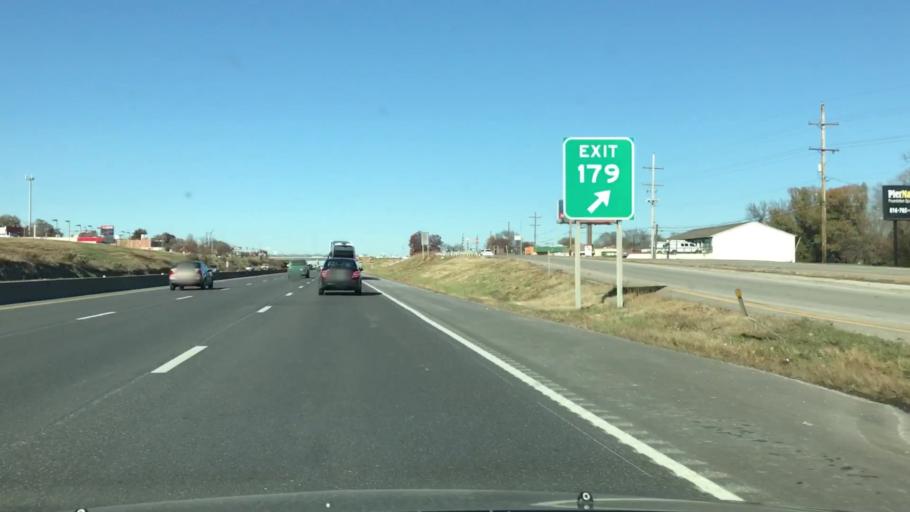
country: US
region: Missouri
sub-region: Jackson County
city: Grandview
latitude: 38.8838
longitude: -94.5254
